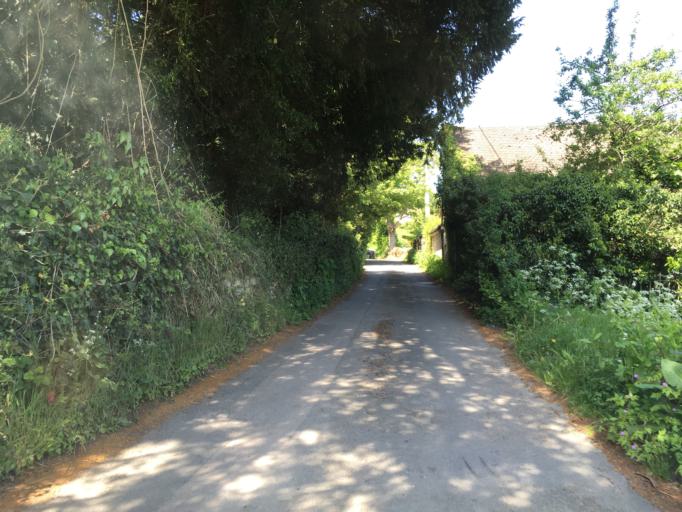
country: GB
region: England
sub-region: Gloucestershire
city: Minchinhampton
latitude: 51.6931
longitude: -2.1936
